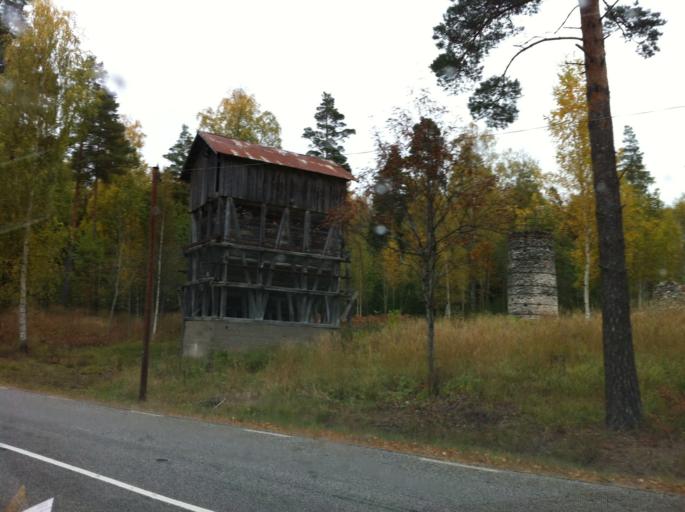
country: SE
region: OErebro
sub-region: Lindesbergs Kommun
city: Stora
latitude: 59.6440
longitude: 15.0522
